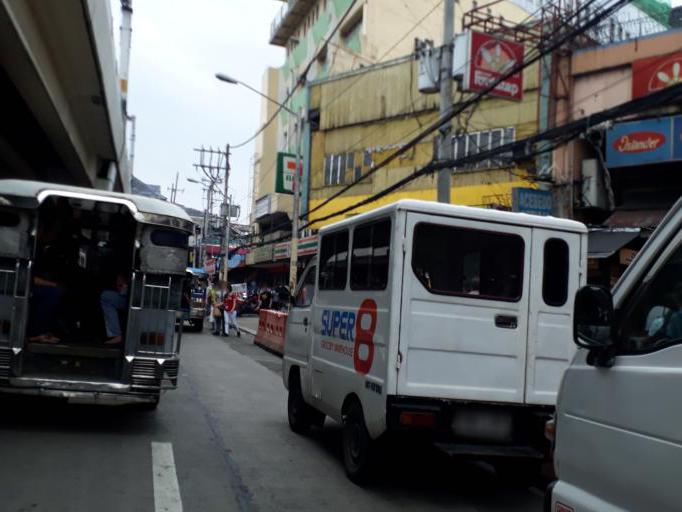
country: PH
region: Metro Manila
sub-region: Caloocan City
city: Niugan
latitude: 14.6555
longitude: 120.9839
